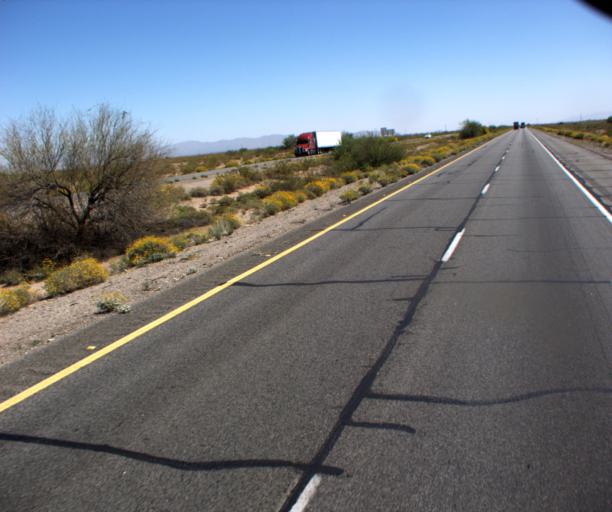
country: US
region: Arizona
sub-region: Maricopa County
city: Buckeye
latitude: 33.4772
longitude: -112.8472
